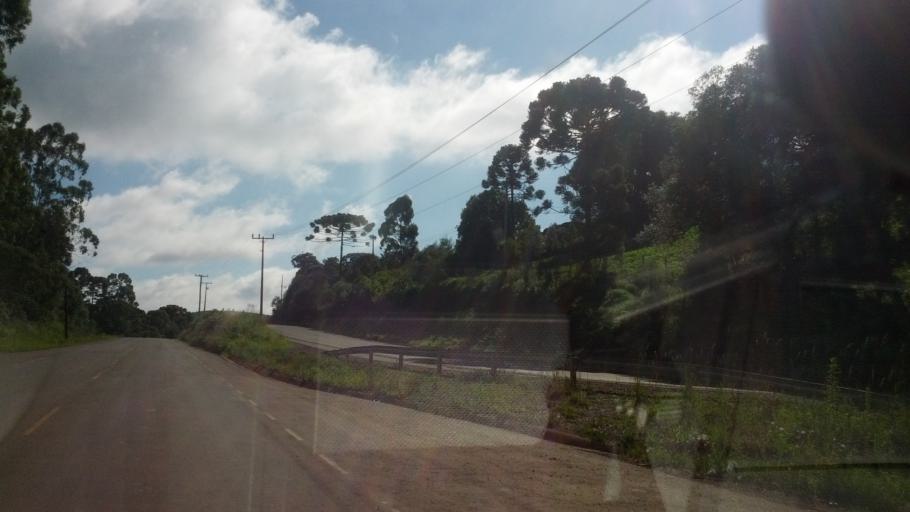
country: BR
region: Rio Grande do Sul
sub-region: Vacaria
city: Estrela
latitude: -27.9019
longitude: -50.7492
